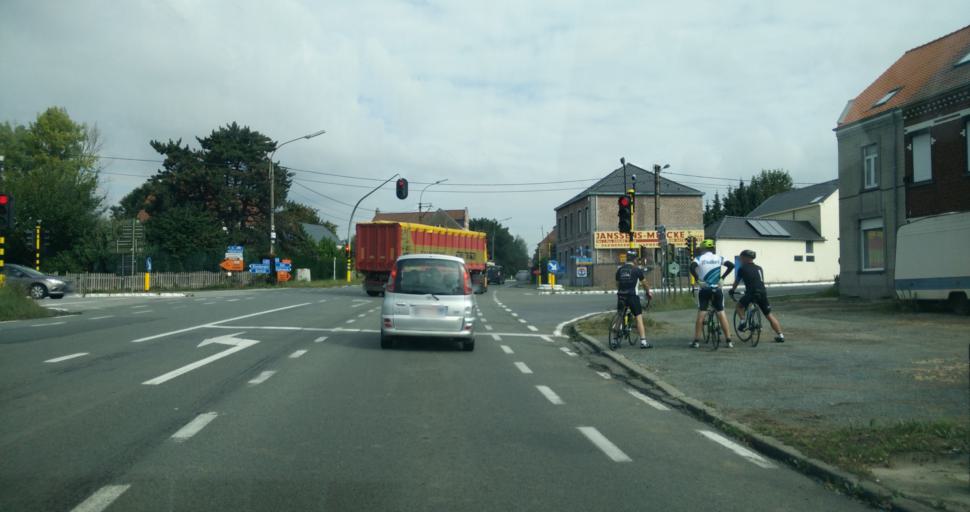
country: BE
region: Flanders
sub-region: Provincie Oost-Vlaanderen
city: Ronse
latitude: 50.7644
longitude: 3.5869
